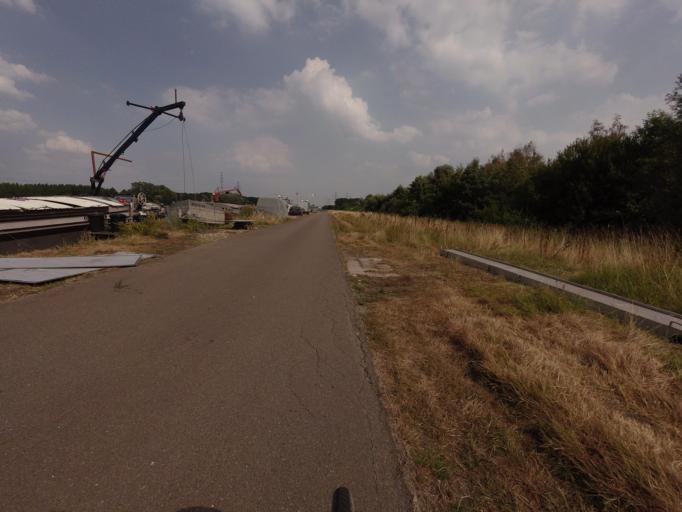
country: BE
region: Flanders
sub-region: Provincie Antwerpen
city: Schilde
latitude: 51.2019
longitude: 4.6136
